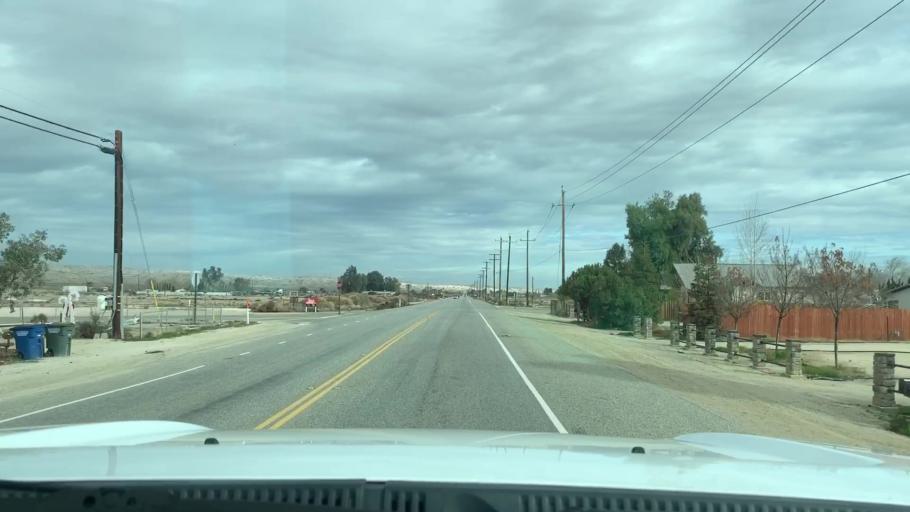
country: US
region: California
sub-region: Kern County
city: Ford City
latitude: 35.2093
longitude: -119.4056
